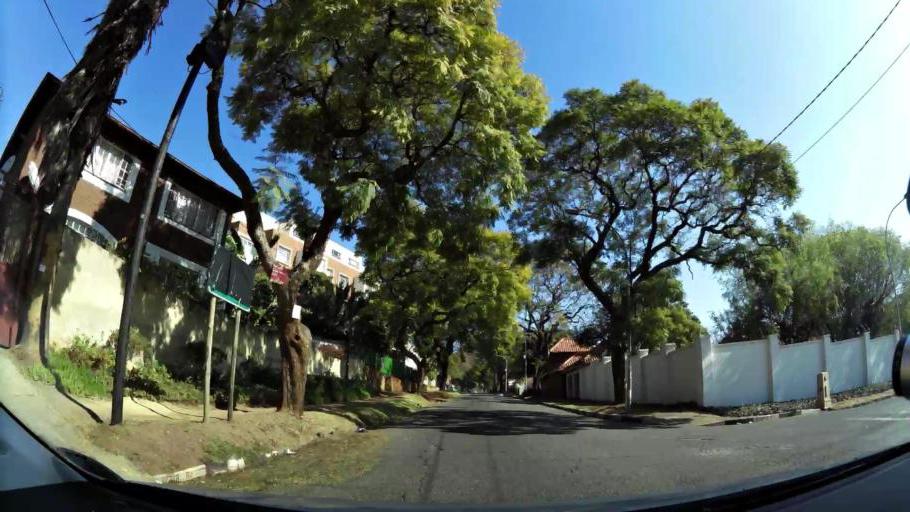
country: ZA
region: Gauteng
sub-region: City of Johannesburg Metropolitan Municipality
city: Johannesburg
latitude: -26.1743
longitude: 28.0702
